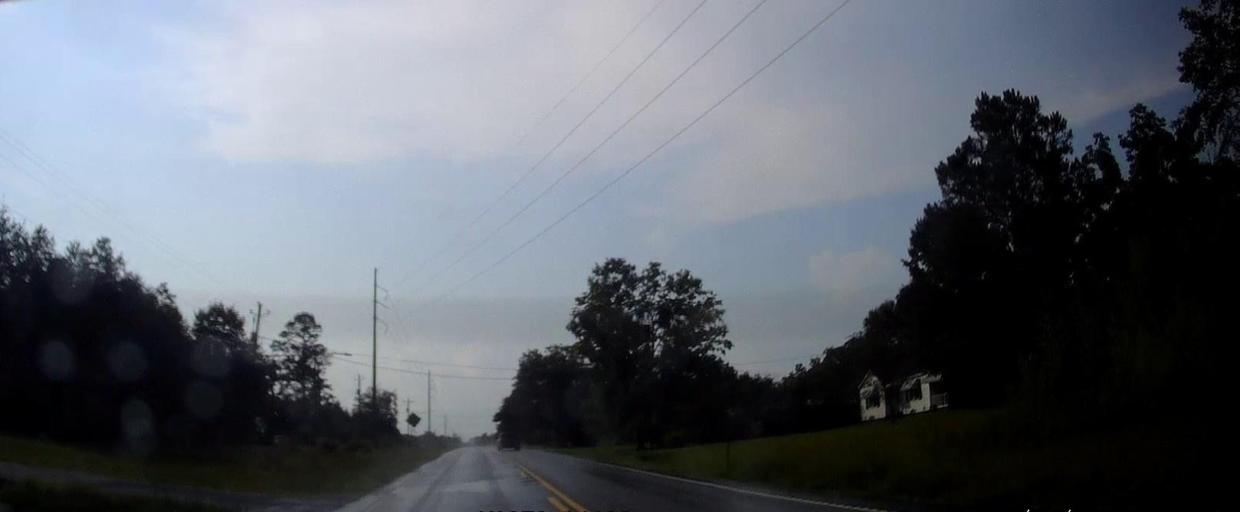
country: US
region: Georgia
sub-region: Twiggs County
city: Jeffersonville
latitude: 32.5934
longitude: -83.2307
